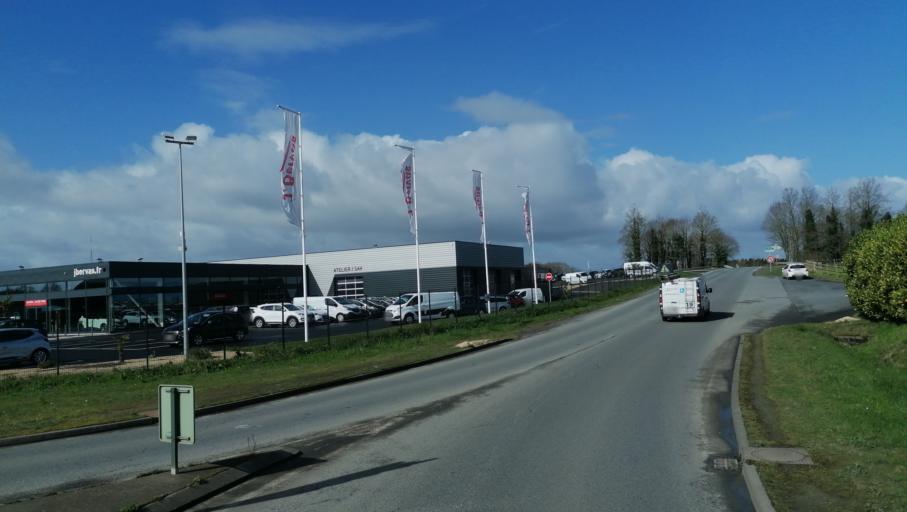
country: FR
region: Brittany
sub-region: Departement des Cotes-d'Armor
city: Tremuson
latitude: 48.5290
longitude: -2.8562
